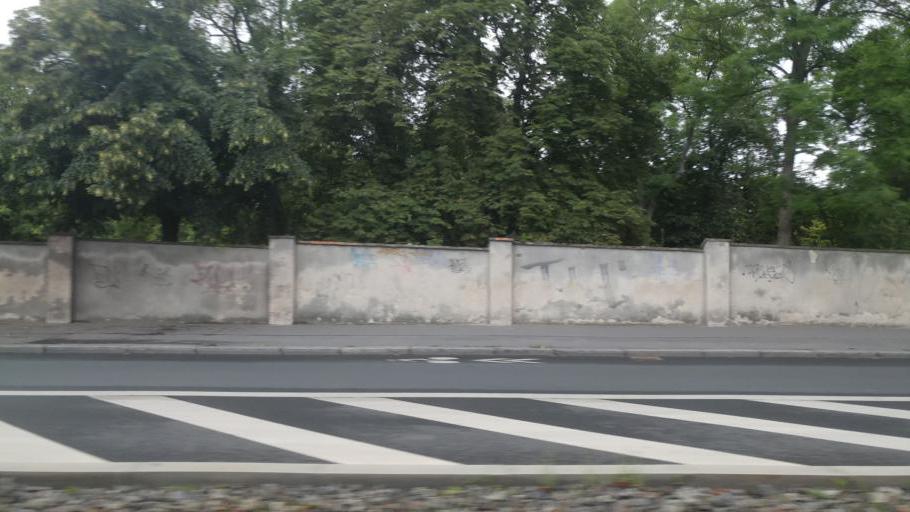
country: CZ
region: Praha
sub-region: Praha 8
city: Liben
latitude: 50.0778
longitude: 14.4796
